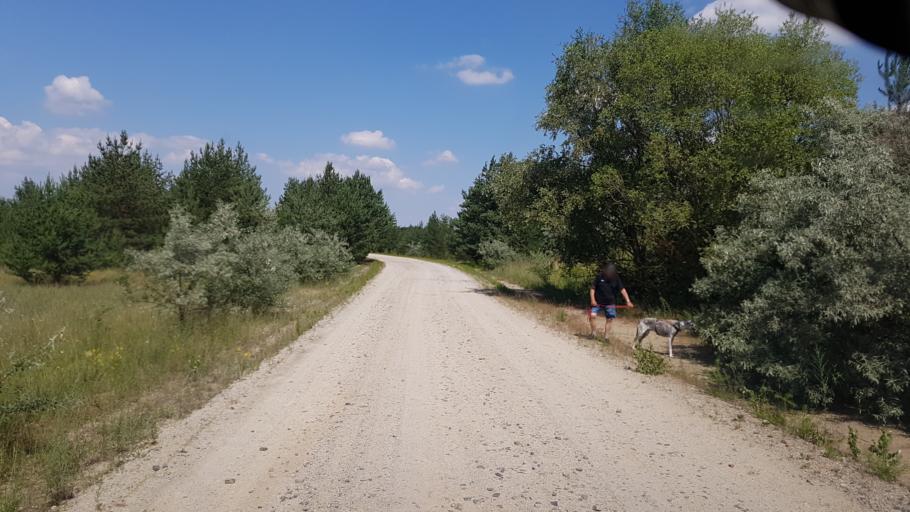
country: DE
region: Brandenburg
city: Lauchhammer
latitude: 51.5552
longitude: 13.7826
